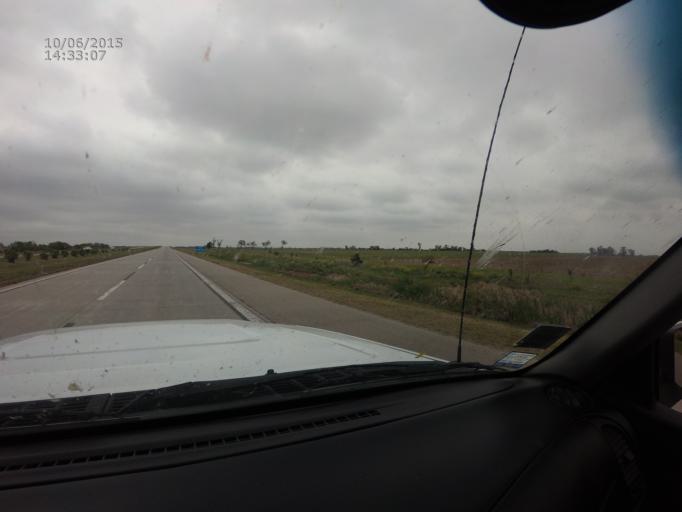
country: AR
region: Cordoba
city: James Craik
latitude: -32.1736
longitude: -63.4026
